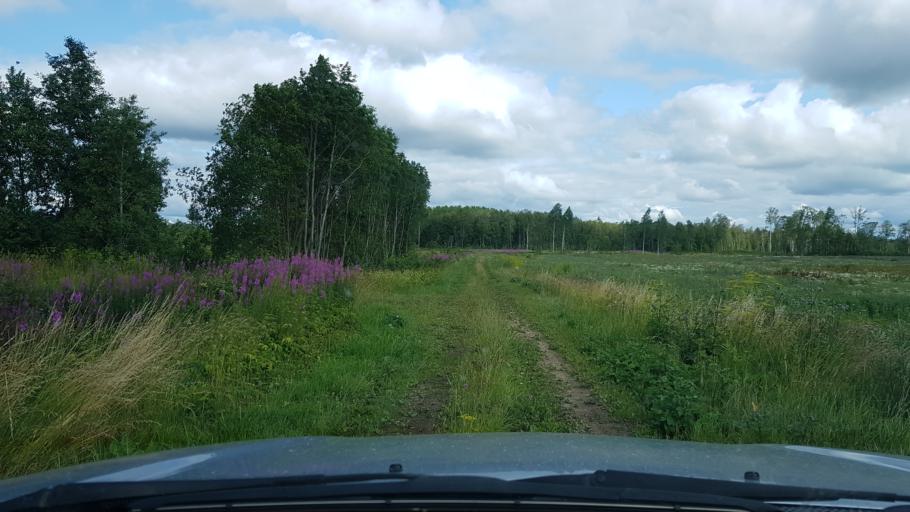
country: EE
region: Ida-Virumaa
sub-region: Narva-Joesuu linn
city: Narva-Joesuu
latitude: 59.3832
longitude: 27.9476
